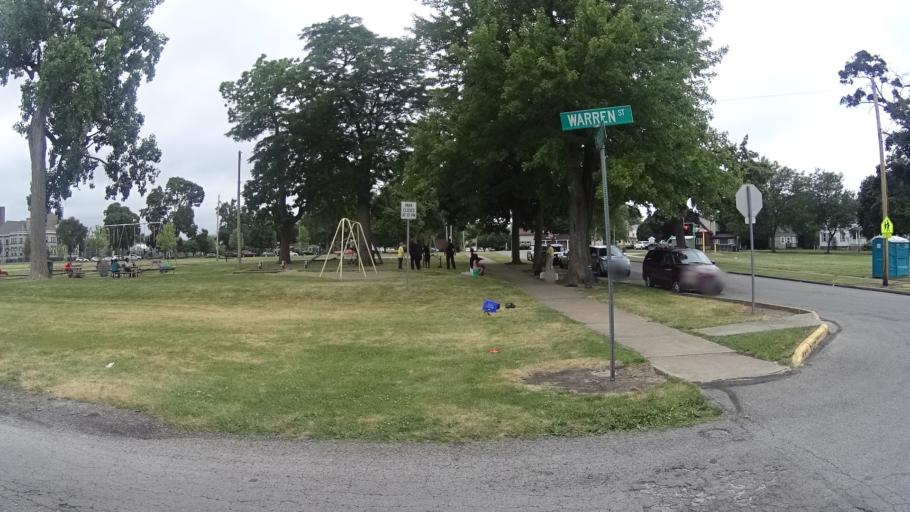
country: US
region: Ohio
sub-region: Erie County
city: Sandusky
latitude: 41.4534
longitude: -82.7025
